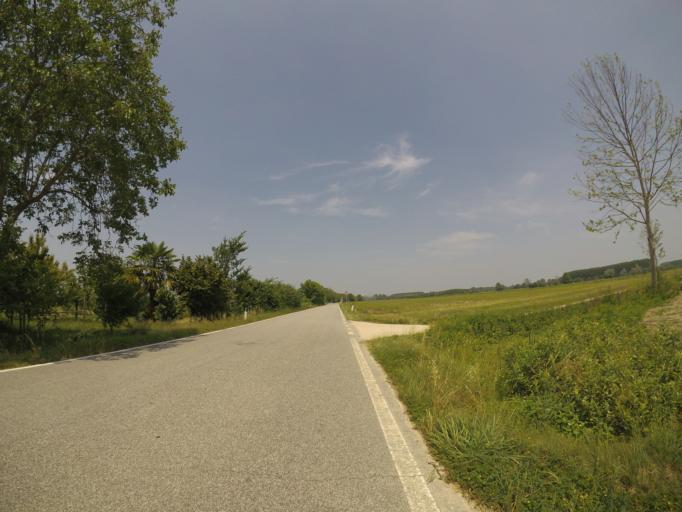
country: IT
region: Friuli Venezia Giulia
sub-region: Provincia di Udine
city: Rivignano
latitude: 45.8558
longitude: 13.0262
